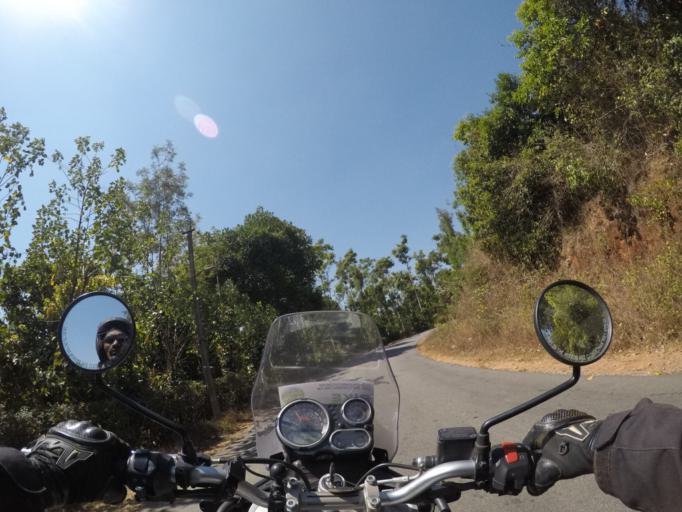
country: IN
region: Karnataka
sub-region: Chikmagalur
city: Mudigere
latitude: 13.0439
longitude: 75.6858
